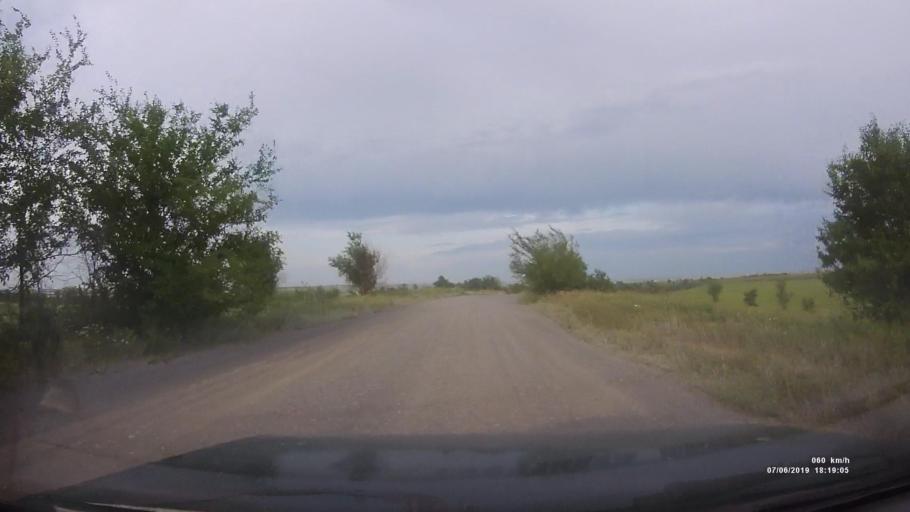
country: RU
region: Rostov
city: Staraya Stanitsa
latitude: 48.2558
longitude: 40.3689
